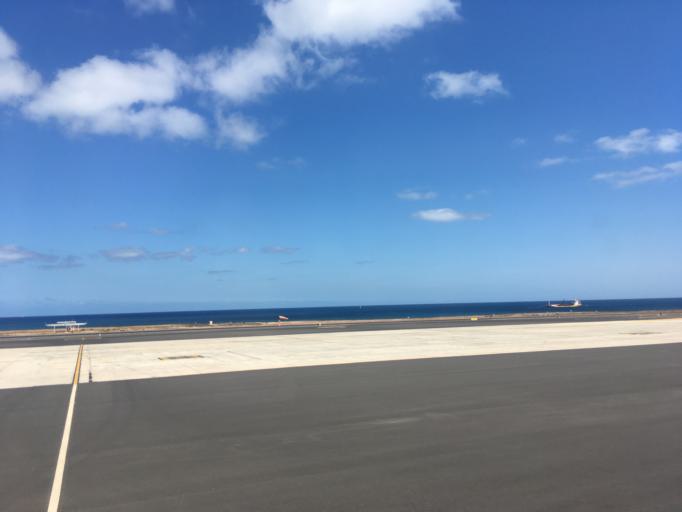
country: ES
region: Canary Islands
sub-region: Provincia de Las Palmas
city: Tias
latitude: 28.9503
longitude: -13.6063
